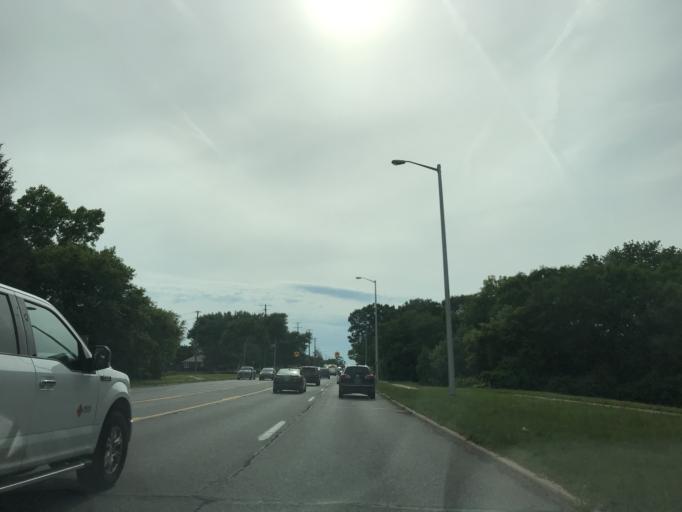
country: US
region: Michigan
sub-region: Oakland County
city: Farmington
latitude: 42.4113
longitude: -83.3919
